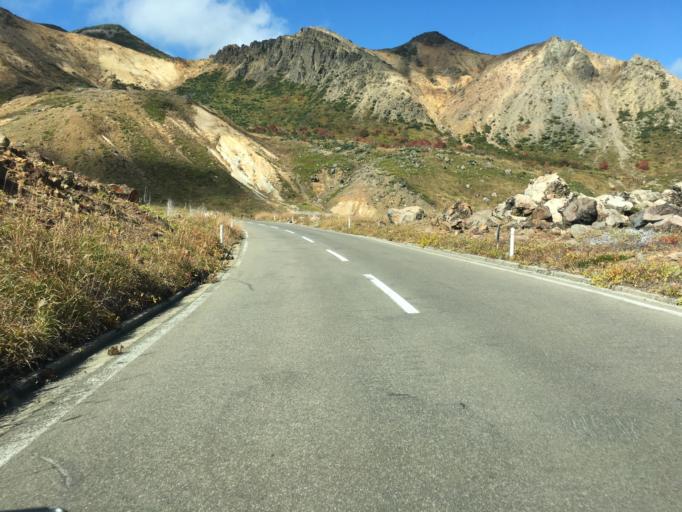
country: JP
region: Fukushima
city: Fukushima-shi
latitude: 37.7298
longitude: 140.2592
